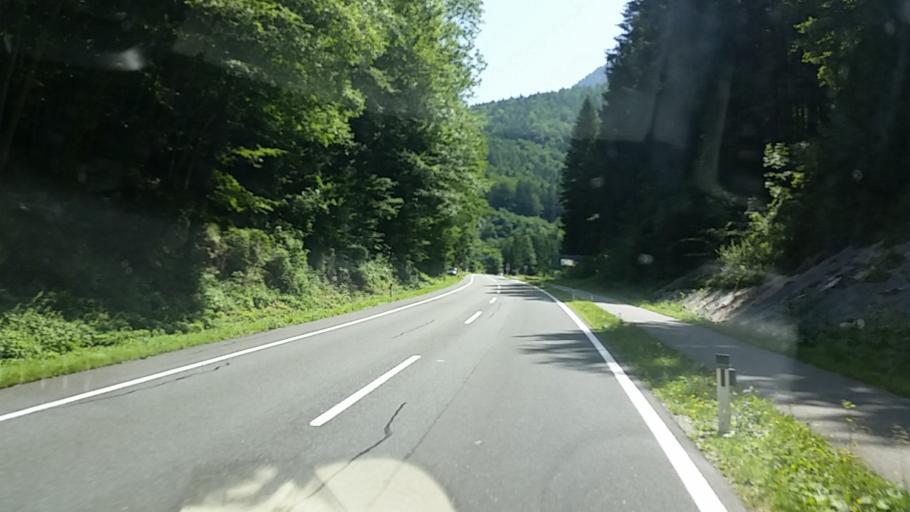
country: AT
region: Salzburg
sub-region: Politischer Bezirk Hallein
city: Scheffau am Tennengebirge
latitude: 47.5787
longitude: 13.1901
